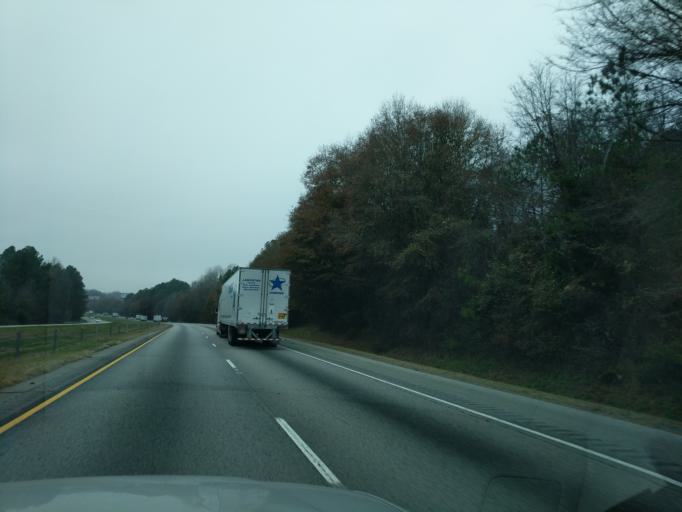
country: US
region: Georgia
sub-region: Franklin County
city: Carnesville
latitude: 34.3665
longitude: -83.2853
